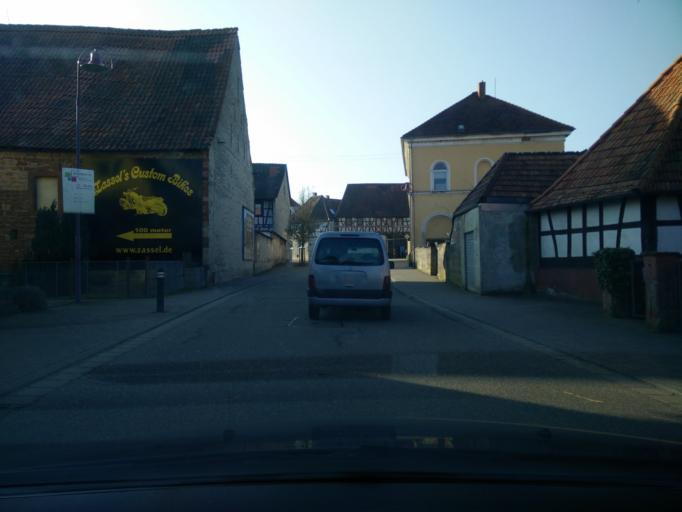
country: DE
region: Rheinland-Pfalz
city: Steinweiler
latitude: 49.1235
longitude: 8.1377
